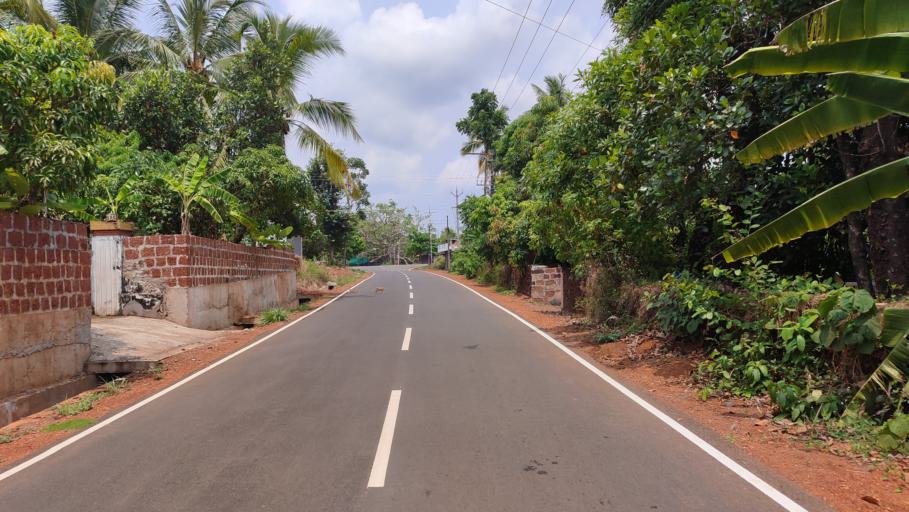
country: IN
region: Kerala
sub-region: Kasaragod District
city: Kannangad
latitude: 12.3224
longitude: 75.1297
